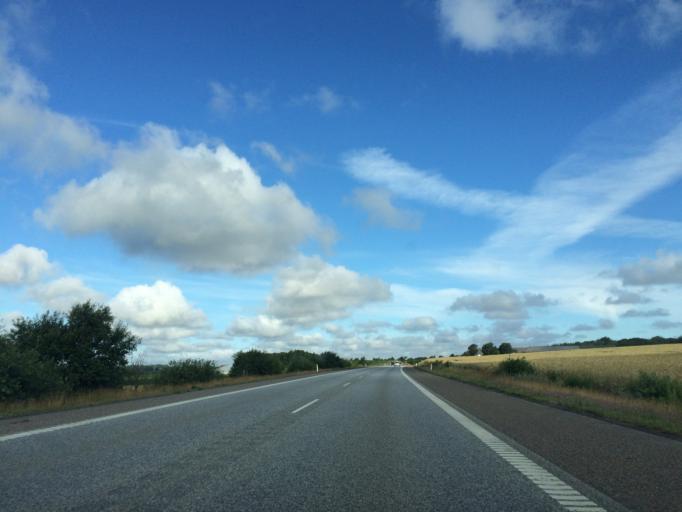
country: DK
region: Central Jutland
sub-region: Silkeborg Kommune
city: Kjellerup
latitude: 56.3691
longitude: 9.4730
